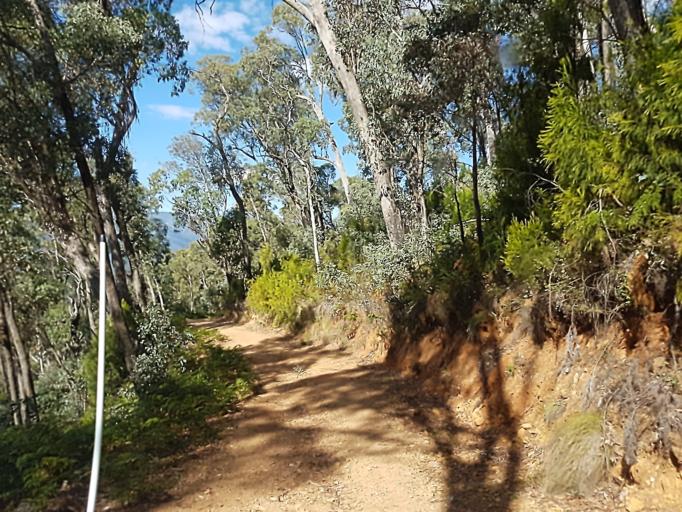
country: AU
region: Victoria
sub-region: Alpine
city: Mount Beauty
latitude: -36.9335
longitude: 147.0025
